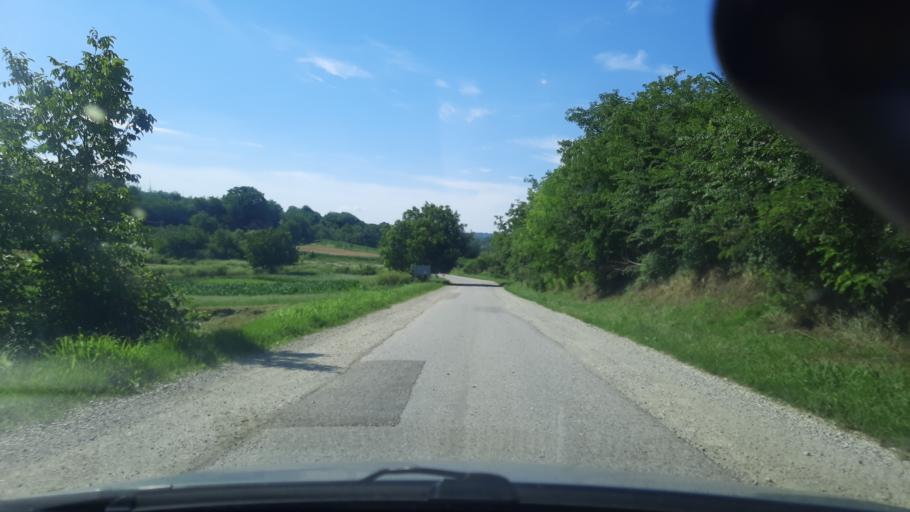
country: RS
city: Cortanovci
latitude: 45.1034
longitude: 19.9891
